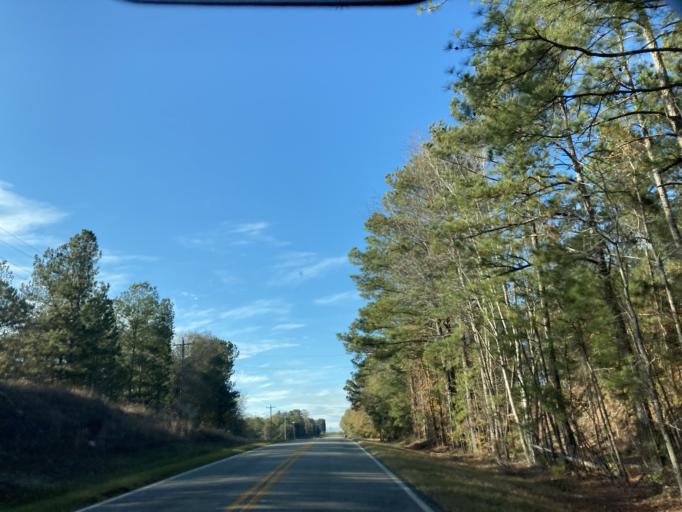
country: US
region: Georgia
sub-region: Jones County
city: Gray
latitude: 32.8905
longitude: -83.5049
